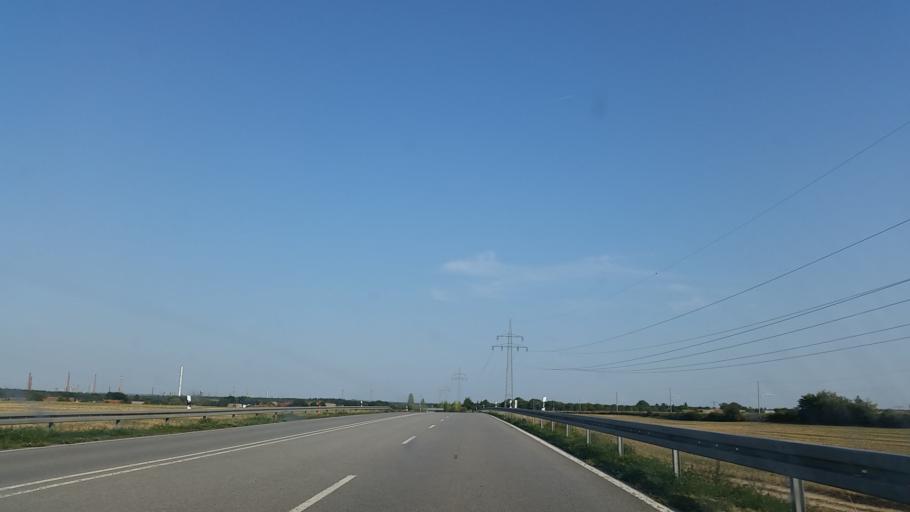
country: DE
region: Brandenburg
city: Meyenburg
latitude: 53.0830
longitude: 14.1895
